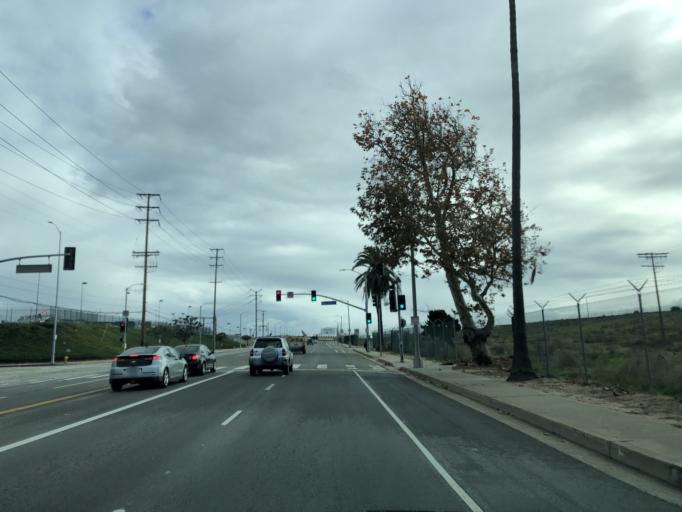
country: US
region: California
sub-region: Los Angeles County
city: Marina del Rey
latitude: 33.9521
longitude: -118.4396
